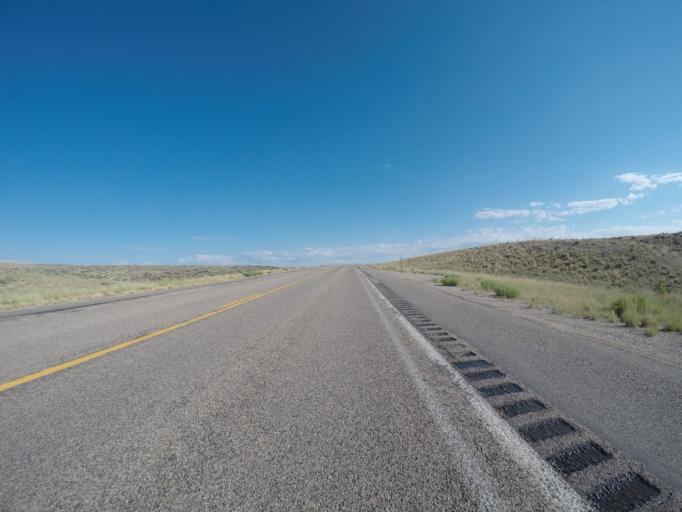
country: US
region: Wyoming
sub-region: Lincoln County
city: Kemmerer
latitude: 42.0482
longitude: -110.1614
